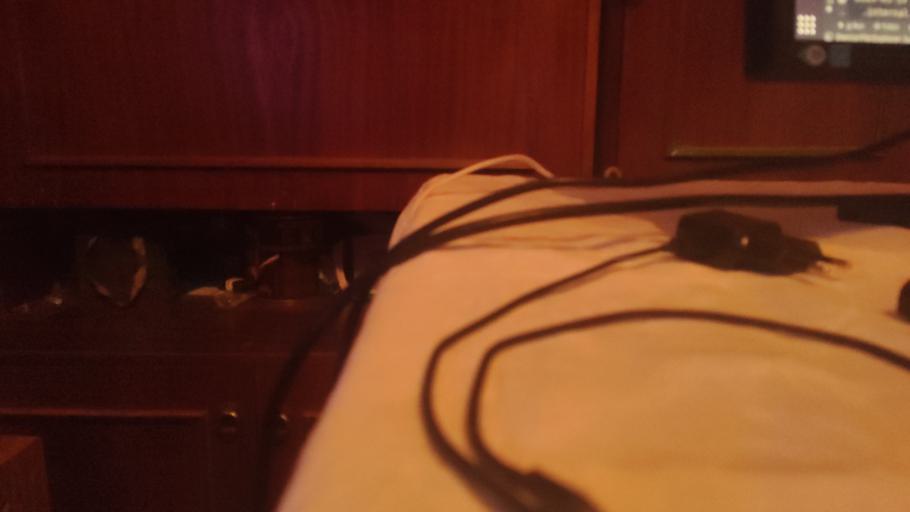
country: RU
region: Moskovskaya
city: Solnechnogorsk
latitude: 56.1865
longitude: 36.9750
